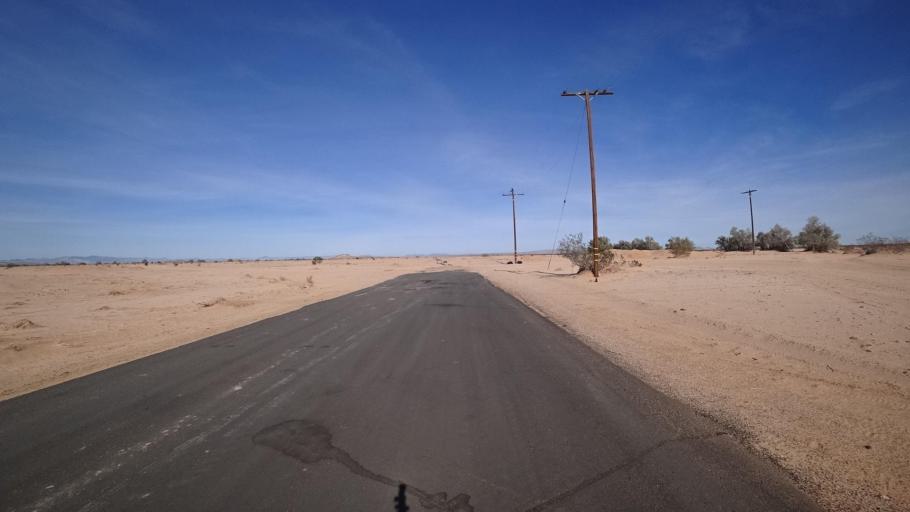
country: US
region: California
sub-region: Kern County
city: North Edwards
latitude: 35.0970
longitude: -117.7927
